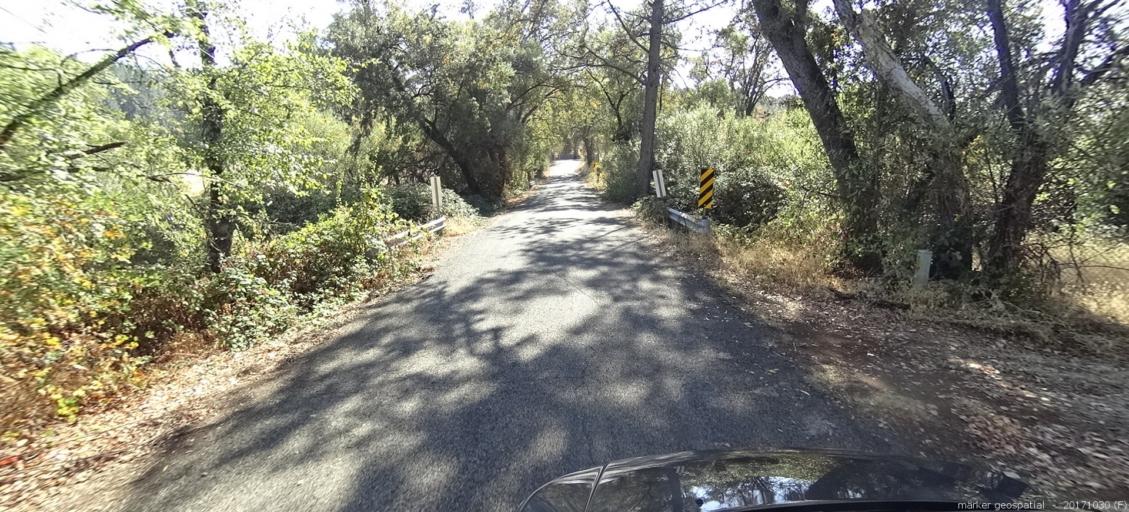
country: US
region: California
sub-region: Shasta County
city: Shingletown
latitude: 40.5149
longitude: -121.9741
